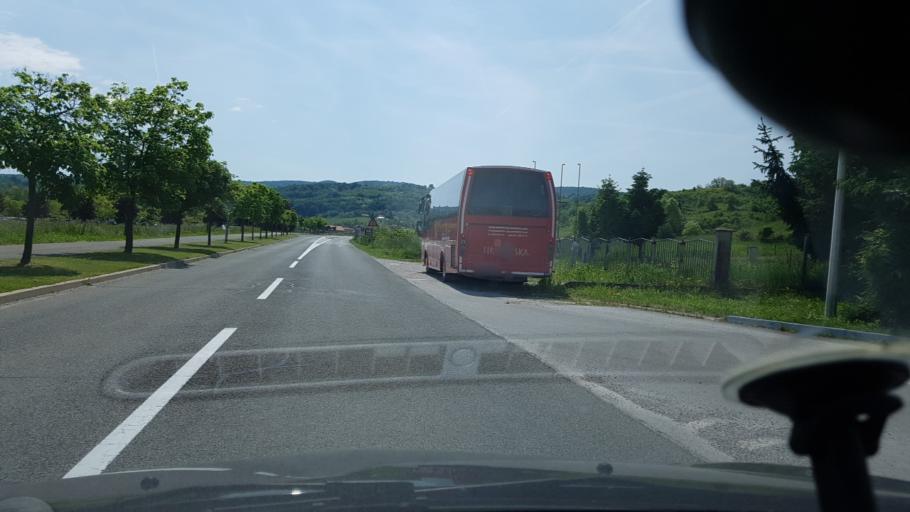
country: HR
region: Krapinsko-Zagorska
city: Marija Bistrica
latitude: 46.0017
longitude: 16.1136
